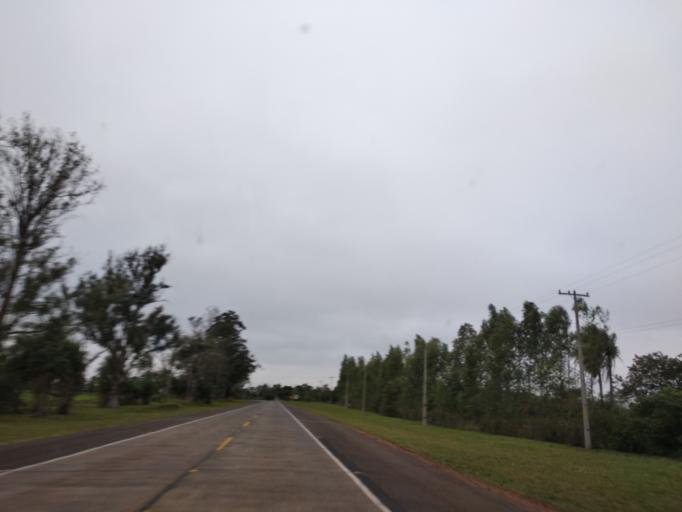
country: PY
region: Misiones
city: Santa Maria
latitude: -26.8778
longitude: -57.0885
